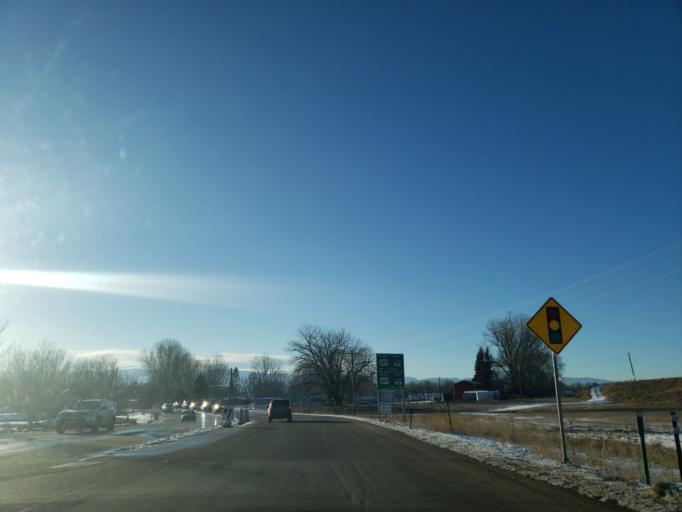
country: US
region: Colorado
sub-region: Larimer County
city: Fort Collins
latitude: 40.6162
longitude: -105.0750
